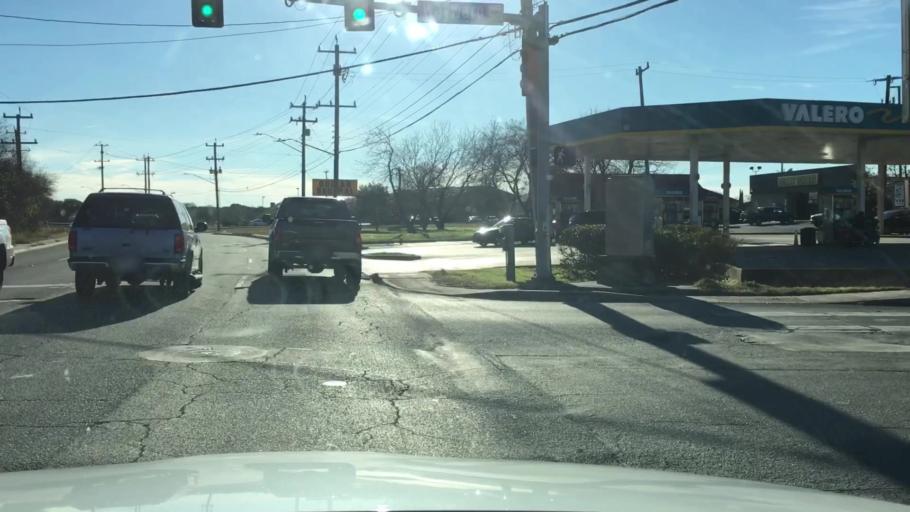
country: US
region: Texas
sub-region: Bexar County
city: Windcrest
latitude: 29.5344
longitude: -98.4287
